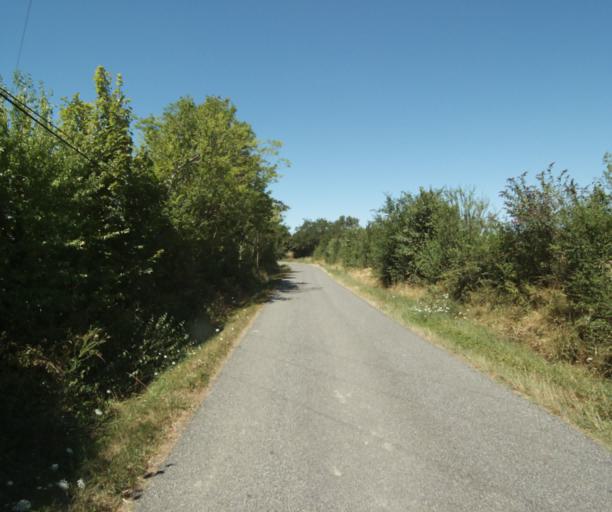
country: FR
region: Midi-Pyrenees
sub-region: Departement de la Haute-Garonne
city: Revel
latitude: 43.4582
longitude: 1.9462
